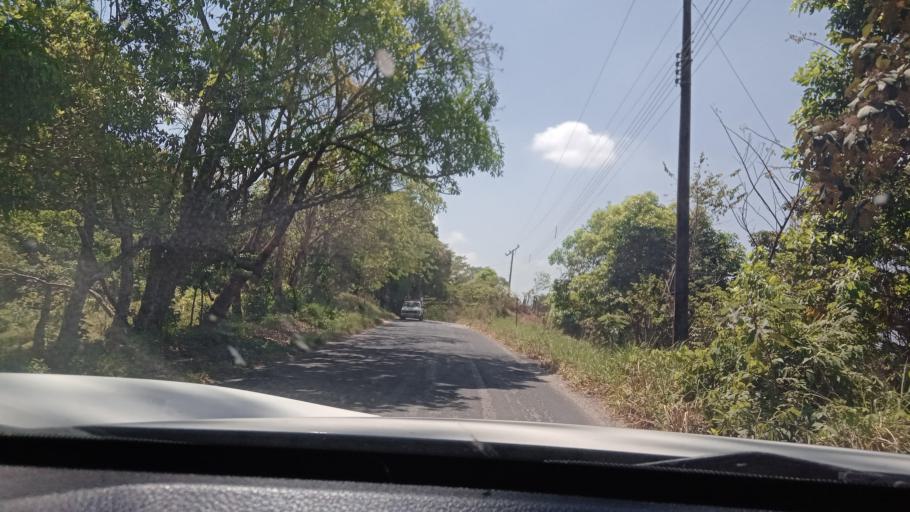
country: MX
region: Veracruz
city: Las Choapas
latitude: 17.7517
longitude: -94.1123
